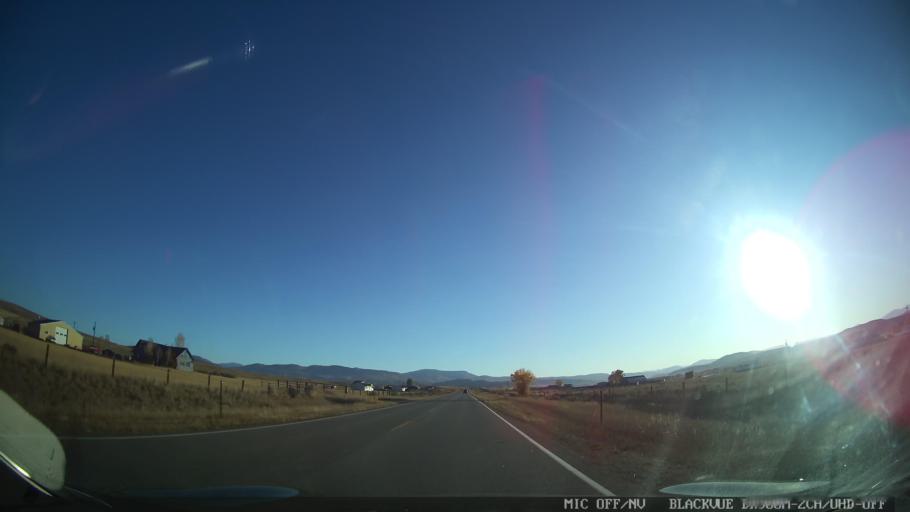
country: US
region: Colorado
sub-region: Grand County
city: Kremmling
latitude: 40.0536
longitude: -106.3340
